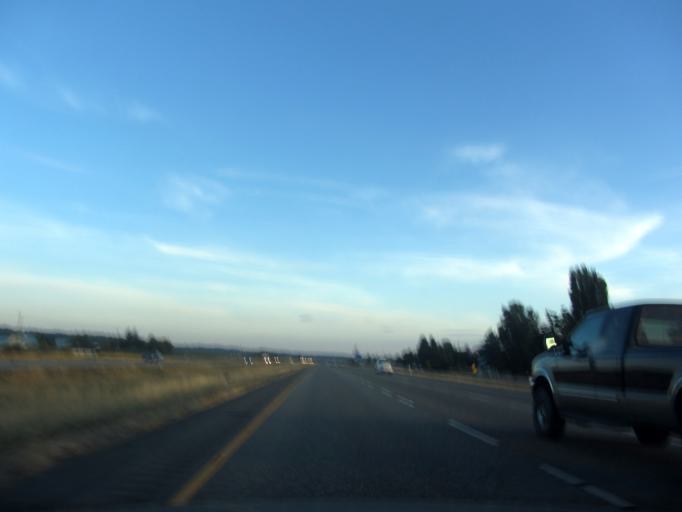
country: US
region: Washington
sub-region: Skagit County
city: Mount Vernon
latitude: 48.3597
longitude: -122.3361
